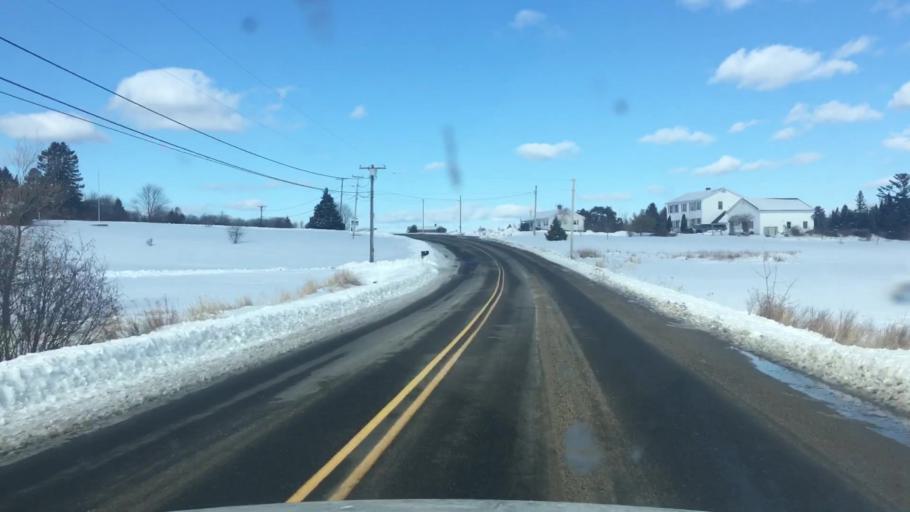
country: US
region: Maine
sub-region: Washington County
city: Machias
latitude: 44.6957
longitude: -67.4673
